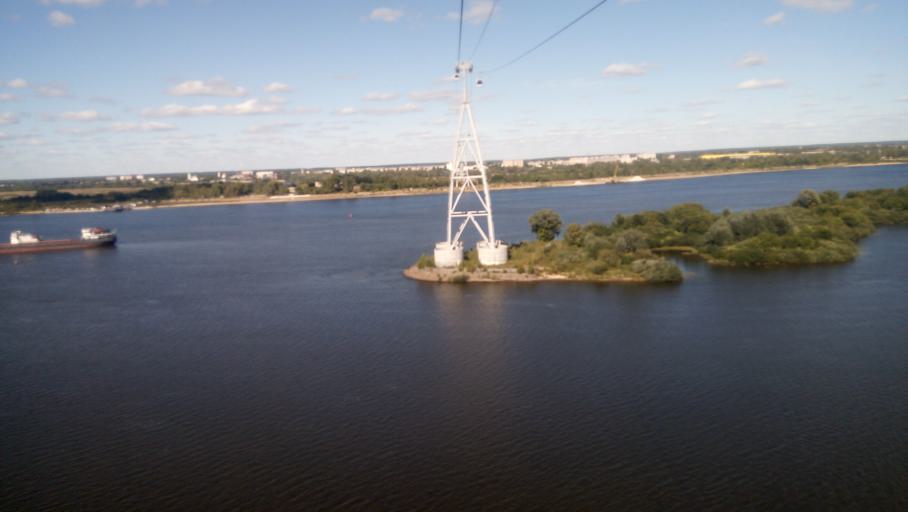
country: RU
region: Nizjnij Novgorod
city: Bor
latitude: 56.3311
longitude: 44.0445
